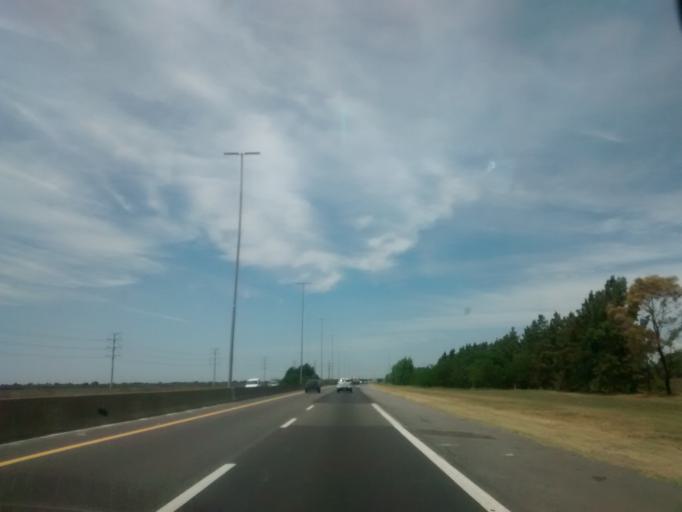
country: AR
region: Buenos Aires
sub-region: Partido de Quilmes
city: Quilmes
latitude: -34.7942
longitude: -58.1350
